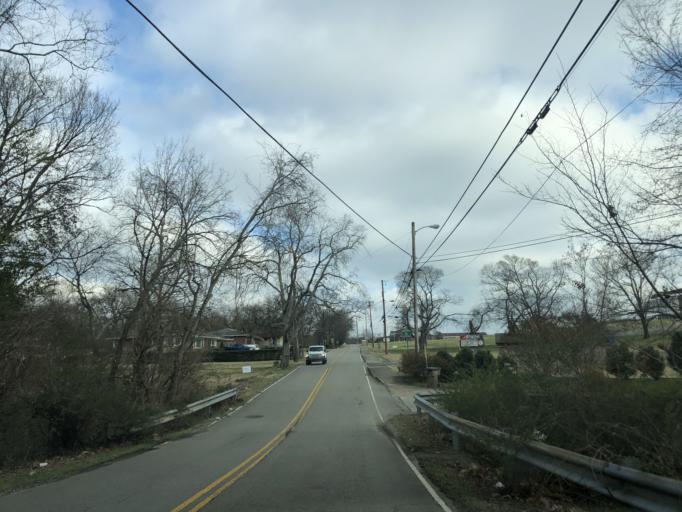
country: US
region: Tennessee
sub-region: Davidson County
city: Nashville
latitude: 36.2048
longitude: -86.7998
